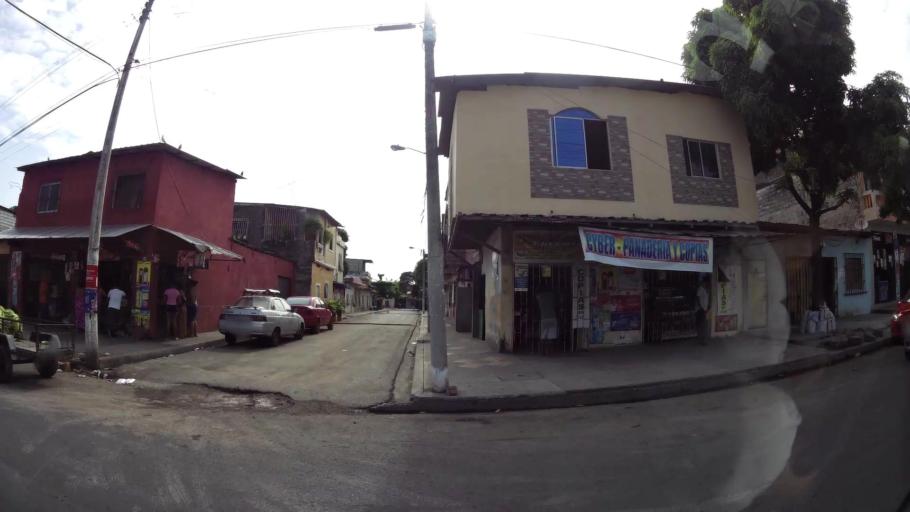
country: EC
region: Guayas
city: Guayaquil
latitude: -2.2503
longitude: -79.8787
